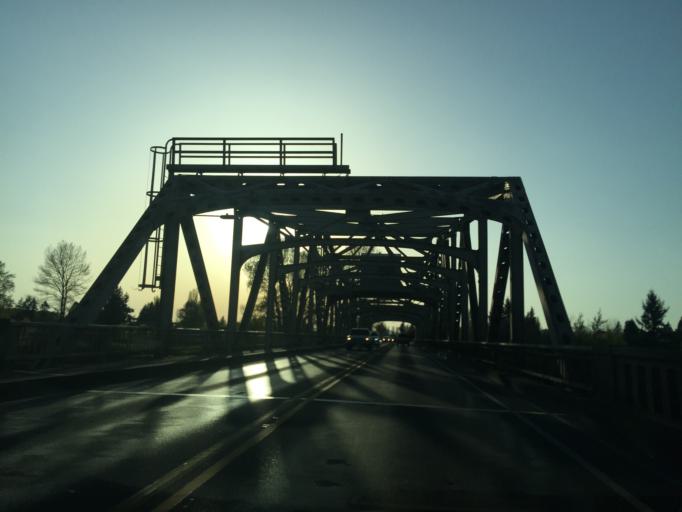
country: US
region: Washington
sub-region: Skagit County
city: Mount Vernon
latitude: 48.4213
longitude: -122.3386
